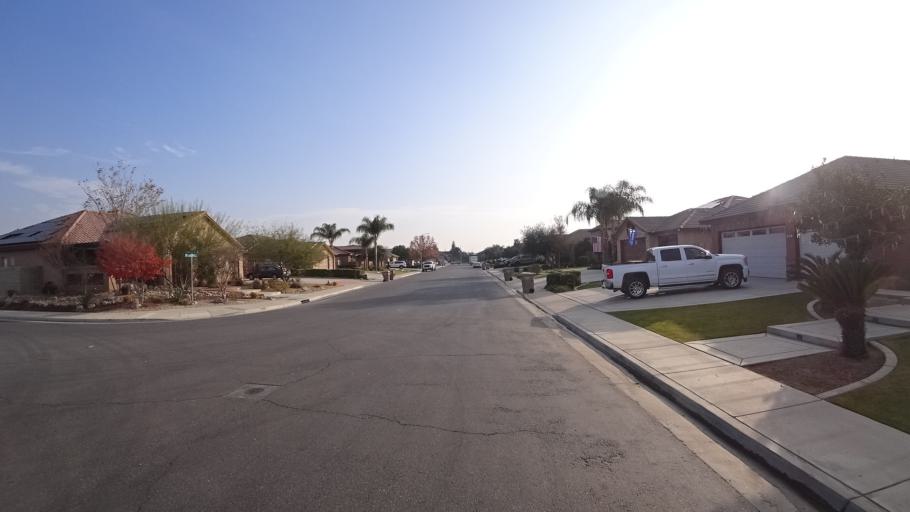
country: US
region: California
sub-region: Kern County
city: Greenacres
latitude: 35.4329
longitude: -119.1125
